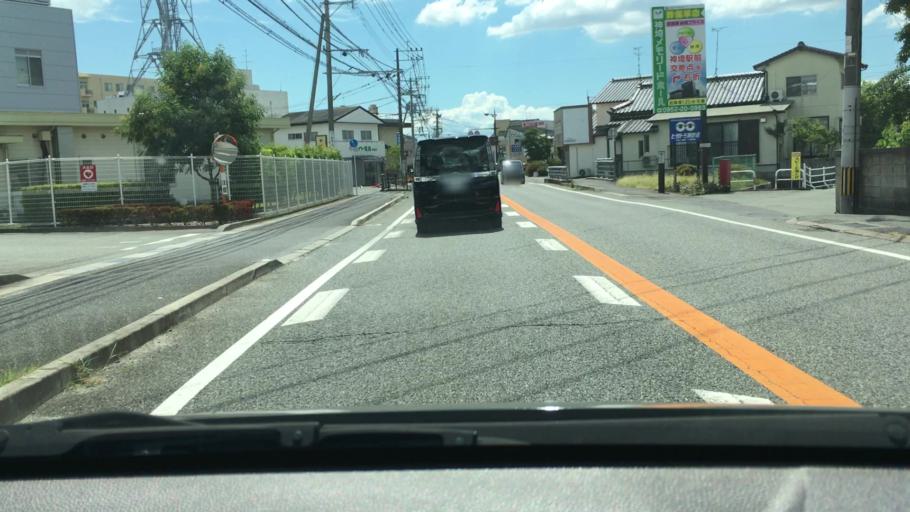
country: JP
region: Saga Prefecture
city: Kanzakimachi-kanzaki
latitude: 33.3143
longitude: 130.3766
